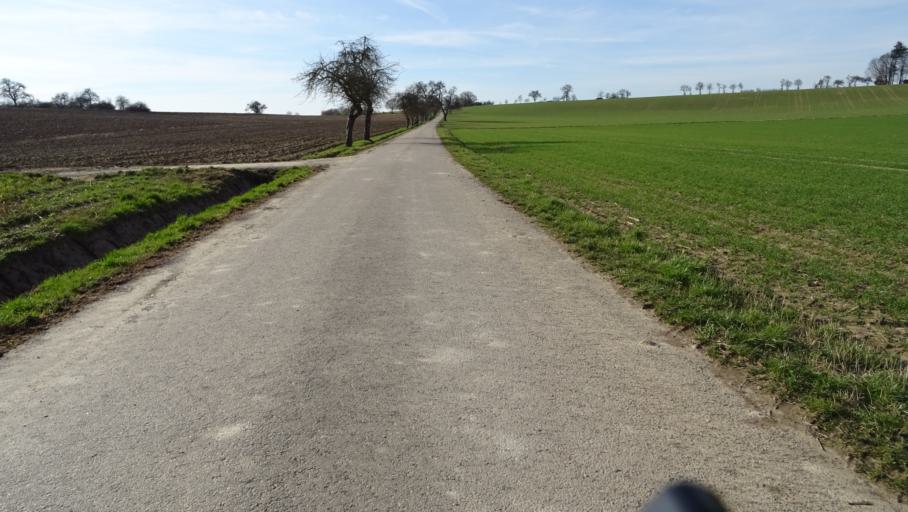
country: DE
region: Baden-Wuerttemberg
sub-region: Karlsruhe Region
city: Seckach
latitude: 49.4118
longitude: 9.3009
